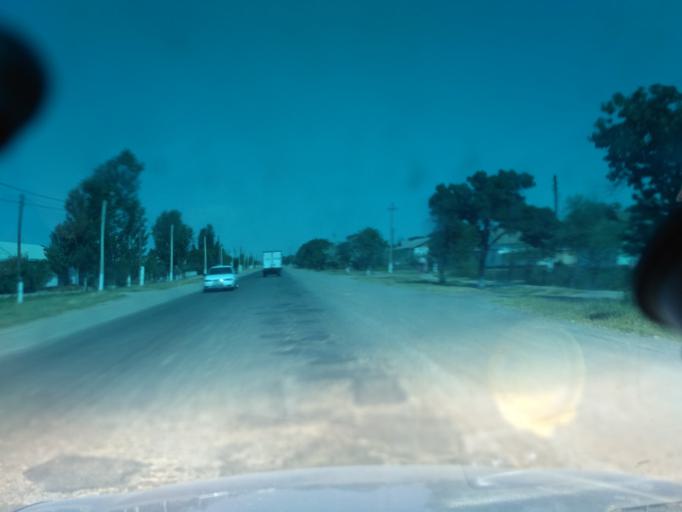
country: UZ
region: Sirdaryo
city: Guliston
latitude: 40.4880
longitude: 68.8759
